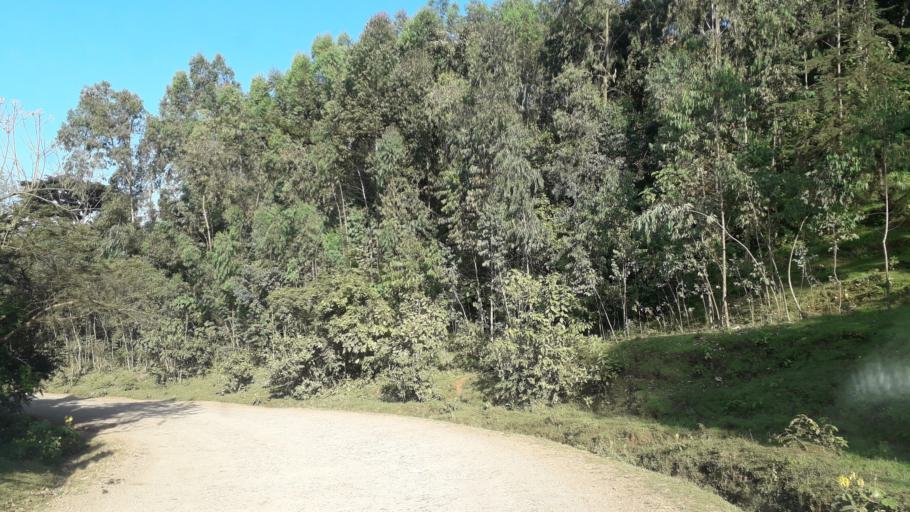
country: ET
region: Oromiya
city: Jima
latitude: 7.4784
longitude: 36.8801
